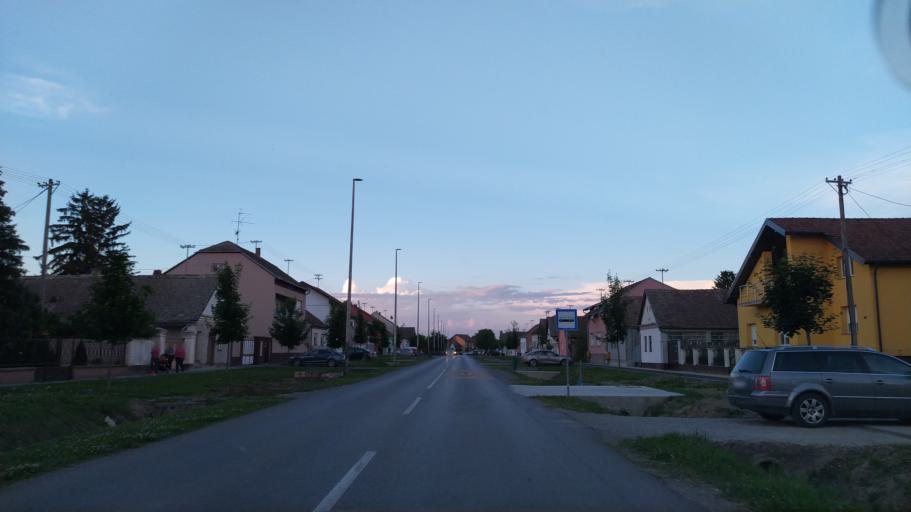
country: HR
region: Osjecko-Baranjska
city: Cepin
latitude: 45.5215
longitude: 18.5570
